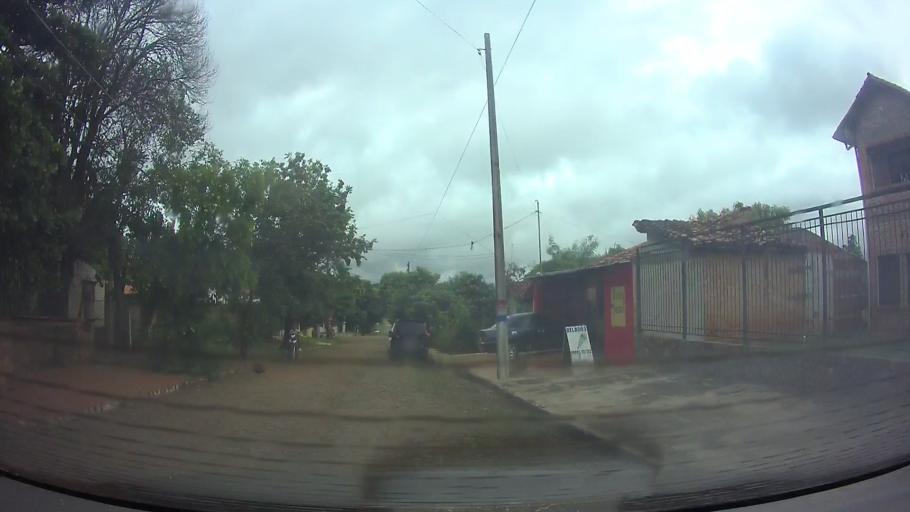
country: PY
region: Cordillera
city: Atyra
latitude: -25.2818
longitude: -57.1729
